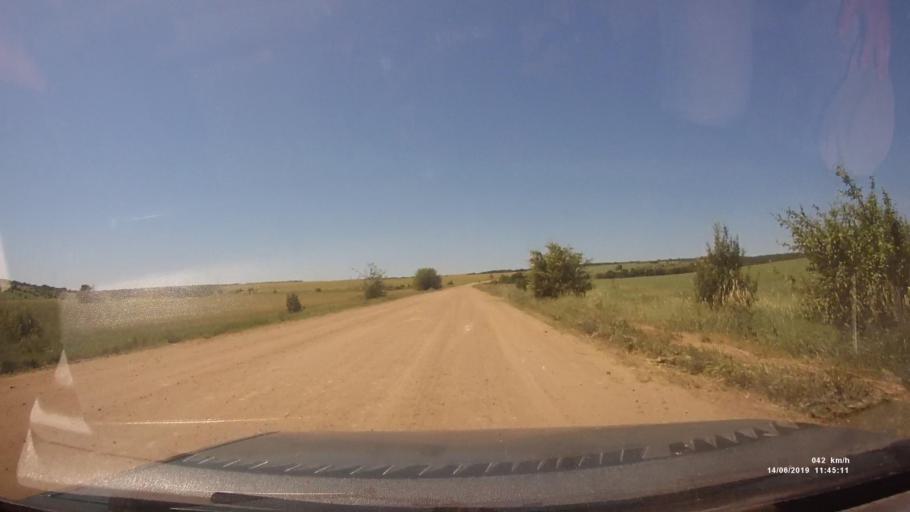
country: RU
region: Rostov
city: Kazanskaya
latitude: 49.8521
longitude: 41.3167
